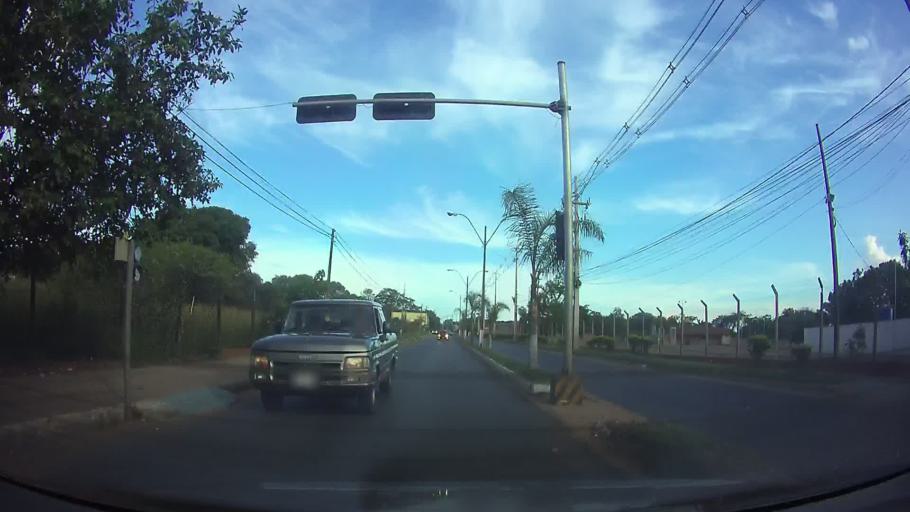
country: PY
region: Central
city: San Antonio
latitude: -25.4215
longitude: -57.5655
